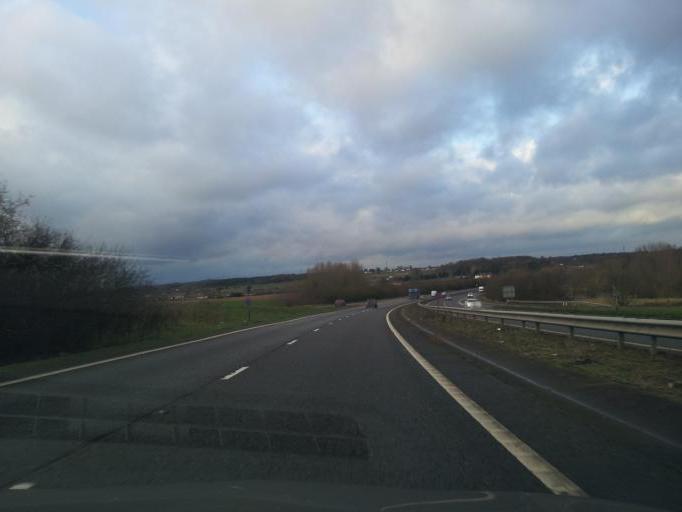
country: GB
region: England
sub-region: Norfolk
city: Bowthorpe
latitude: 52.6267
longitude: 1.1958
